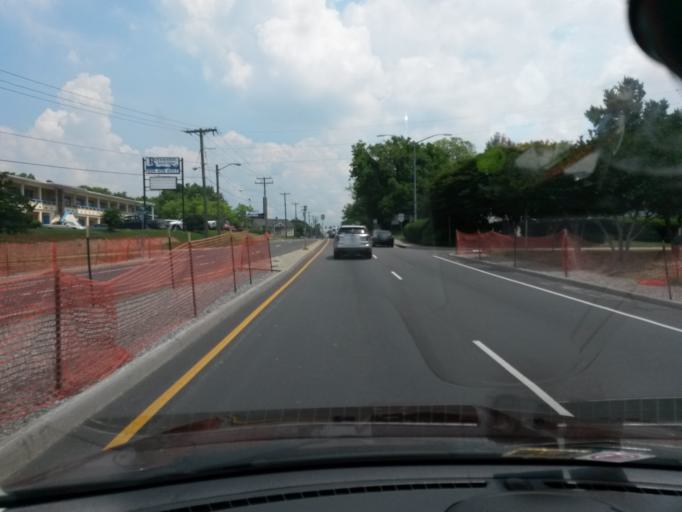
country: US
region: Virginia
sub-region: City of Hopewell
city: Hopewell
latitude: 37.3094
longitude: -77.2956
